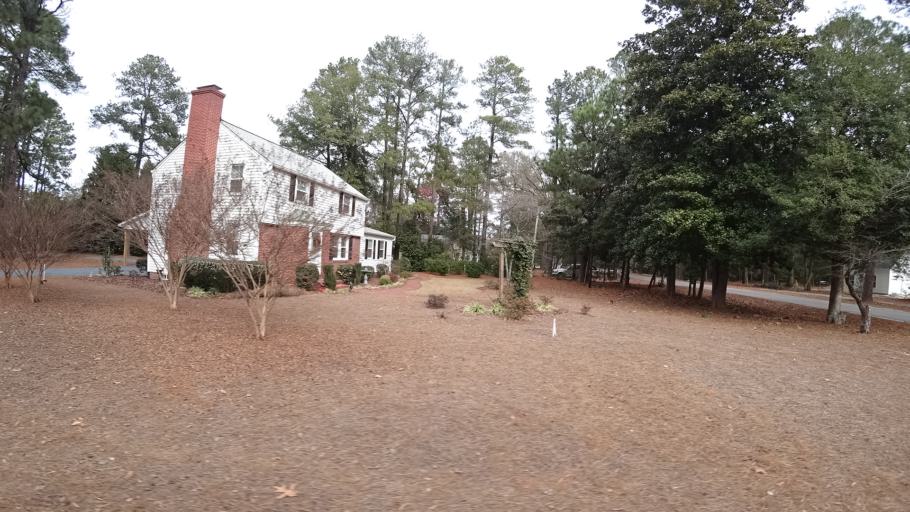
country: US
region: North Carolina
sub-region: Moore County
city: Pinehurst
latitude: 35.2029
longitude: -79.4611
